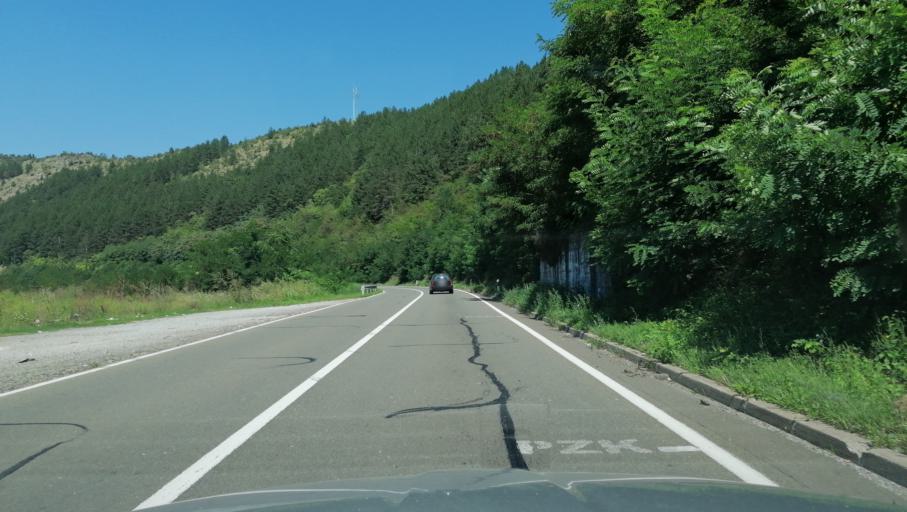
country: RS
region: Central Serbia
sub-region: Raski Okrug
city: Kraljevo
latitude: 43.6624
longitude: 20.5824
